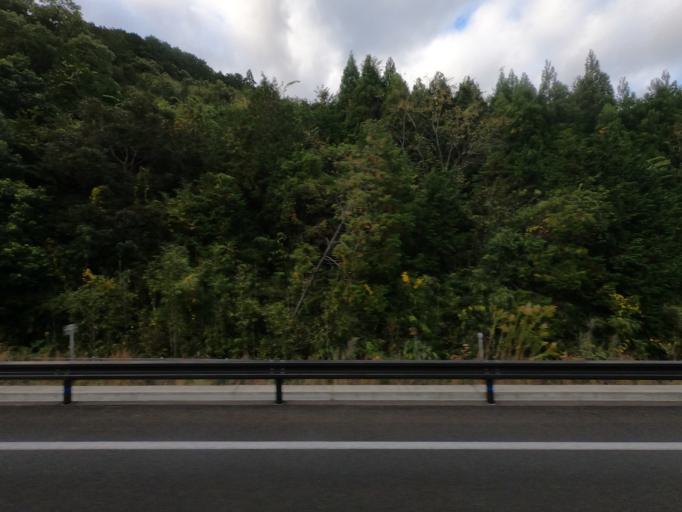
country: JP
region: Kumamoto
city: Minamata
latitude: 32.2354
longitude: 130.4562
